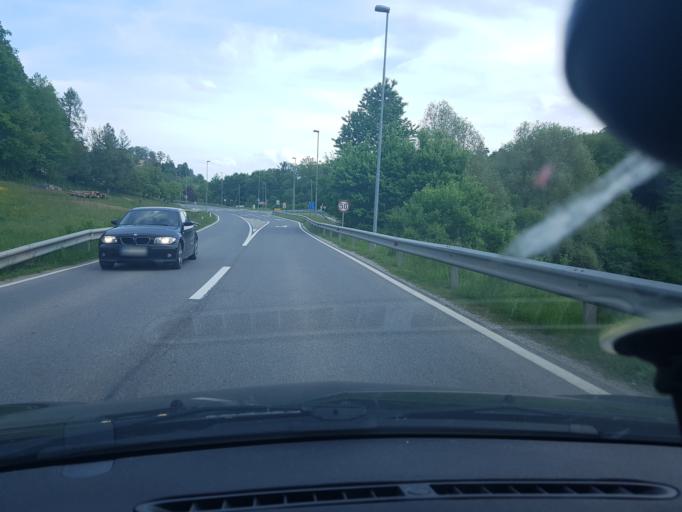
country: SI
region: Rogaska Slatina
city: Rogaska Slatina
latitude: 46.2501
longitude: 15.6383
